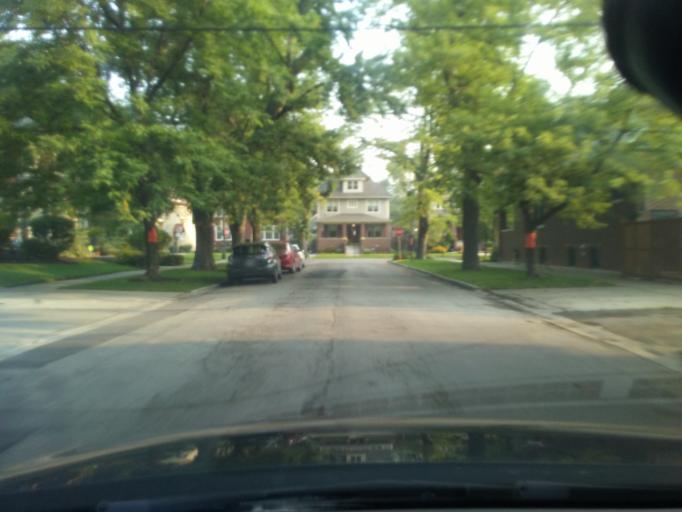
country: US
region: Illinois
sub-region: Cook County
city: Lincolnwood
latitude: 41.9643
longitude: -87.7023
